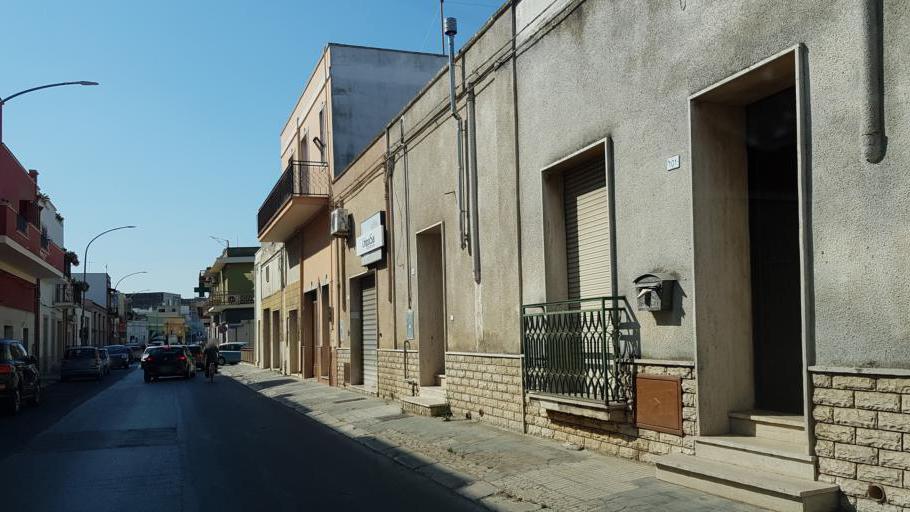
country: IT
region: Apulia
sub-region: Provincia di Brindisi
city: San Donaci
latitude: 40.4490
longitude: 17.9217
